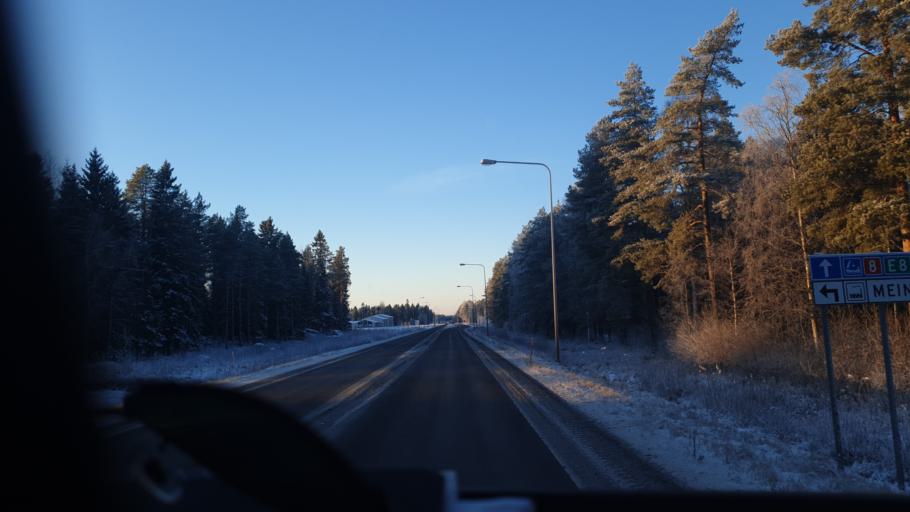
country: FI
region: Northern Ostrobothnia
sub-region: Ylivieska
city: Kalajoki
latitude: 64.2494
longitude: 23.8977
